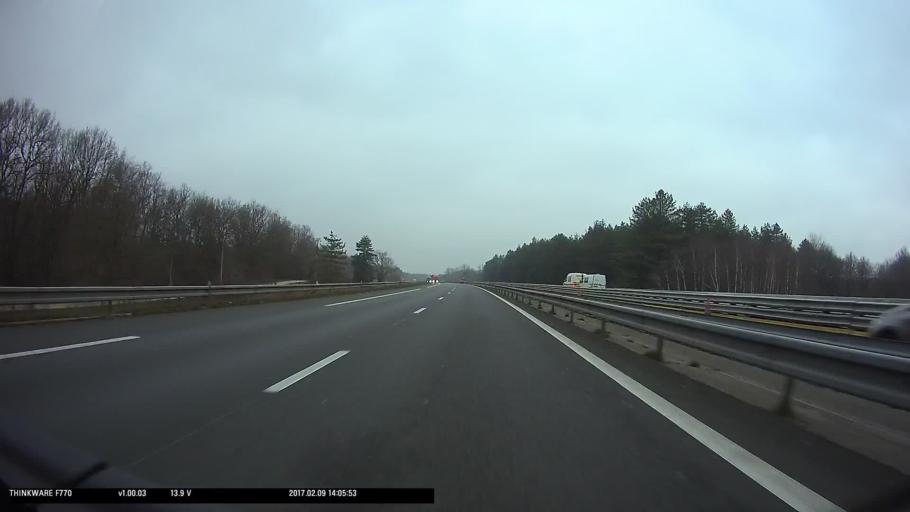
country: FR
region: Centre
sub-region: Departement du Loir-et-Cher
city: Nouan-le-Fuzelier
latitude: 47.5163
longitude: 2.0081
